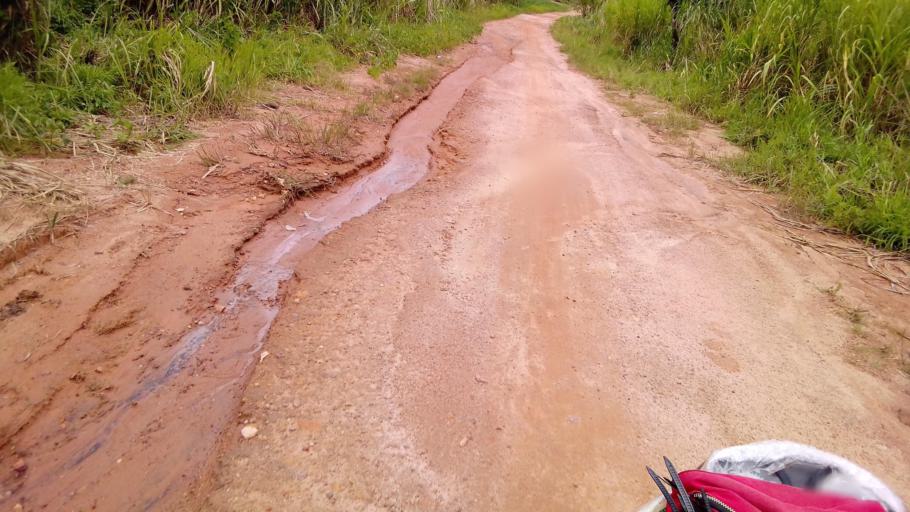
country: SL
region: Eastern Province
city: Koidu
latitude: 8.6867
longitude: -10.9296
